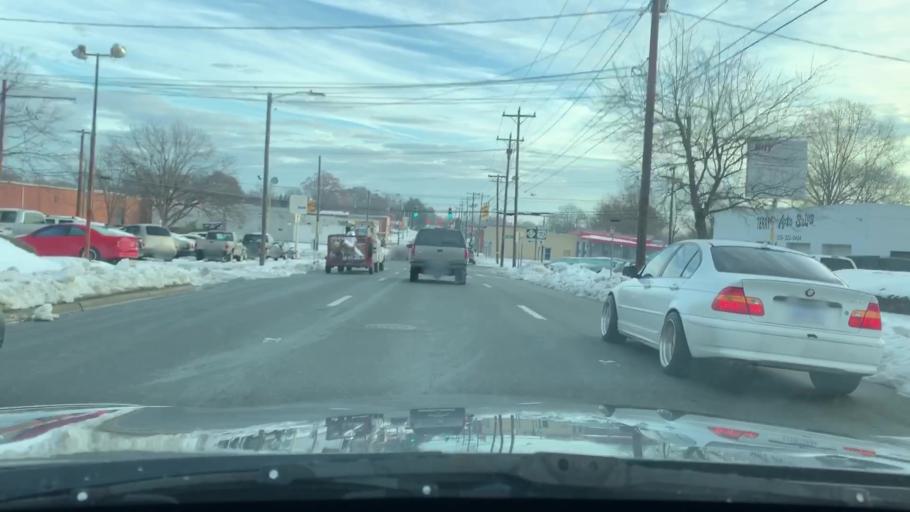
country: US
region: North Carolina
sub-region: Alamance County
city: Burlington
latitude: 36.0988
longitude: -79.4338
